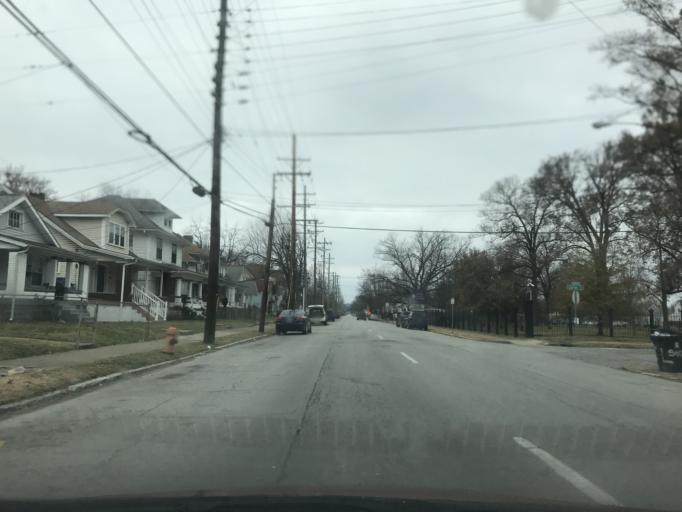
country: US
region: Kentucky
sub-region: Jefferson County
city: Louisville
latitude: 38.2689
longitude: -85.7839
